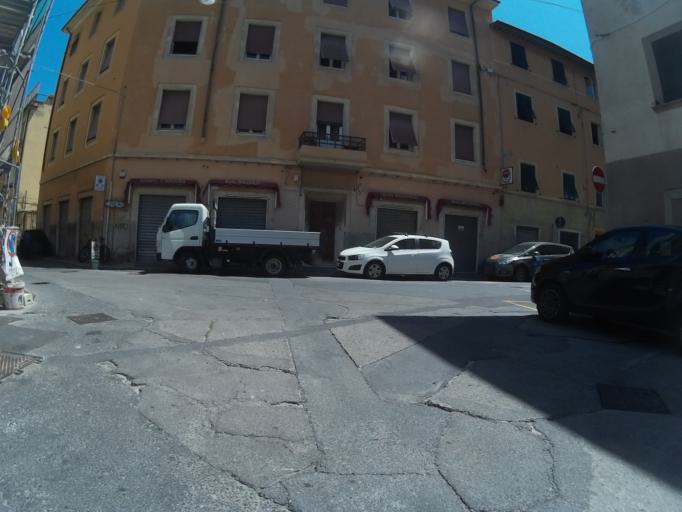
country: IT
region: Tuscany
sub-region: Provincia di Livorno
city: Livorno
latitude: 43.5553
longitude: 10.3144
